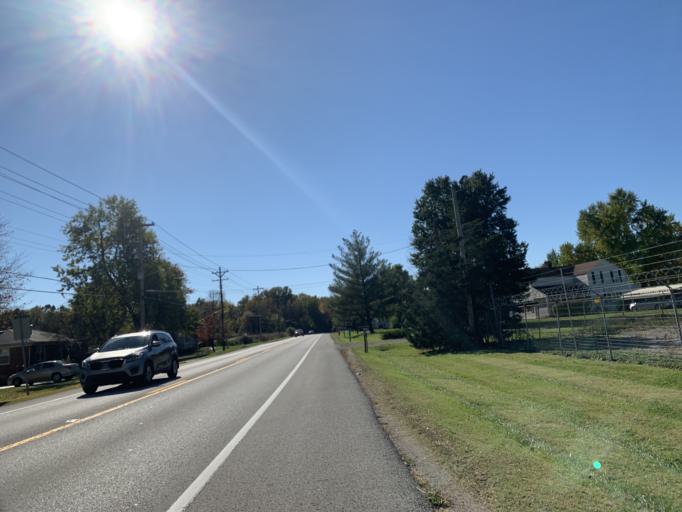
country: US
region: Kentucky
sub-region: Jefferson County
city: Saint Dennis
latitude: 38.2006
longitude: -85.8569
